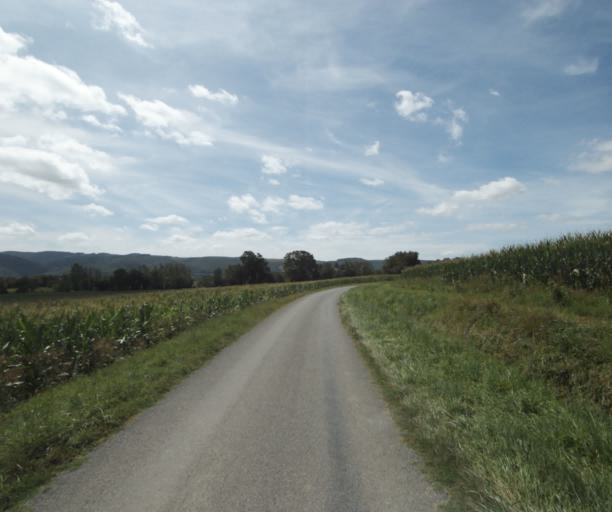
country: FR
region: Midi-Pyrenees
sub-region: Departement du Tarn
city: Soreze
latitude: 43.4839
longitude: 2.0779
